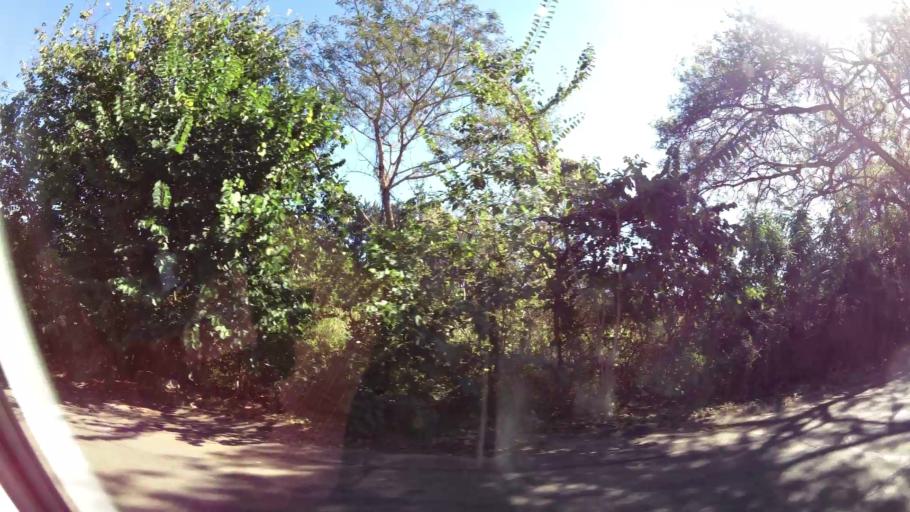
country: ZA
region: Limpopo
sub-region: Mopani District Municipality
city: Tzaneen
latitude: -23.8271
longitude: 30.1548
